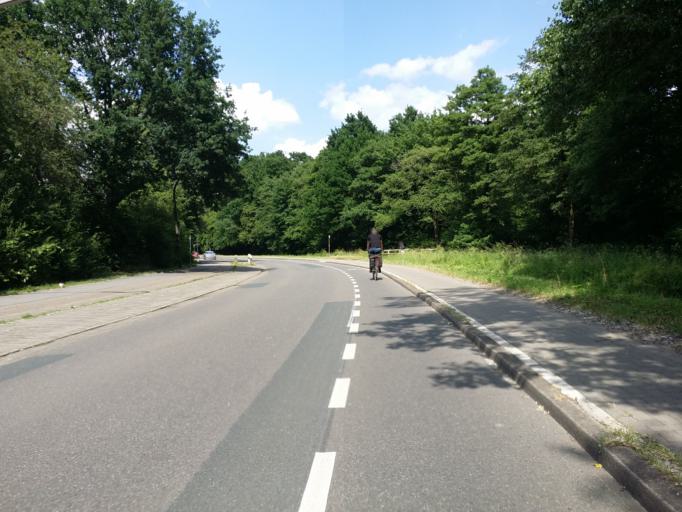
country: DE
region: Lower Saxony
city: Delmenhorst
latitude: 53.0418
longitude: 8.6145
